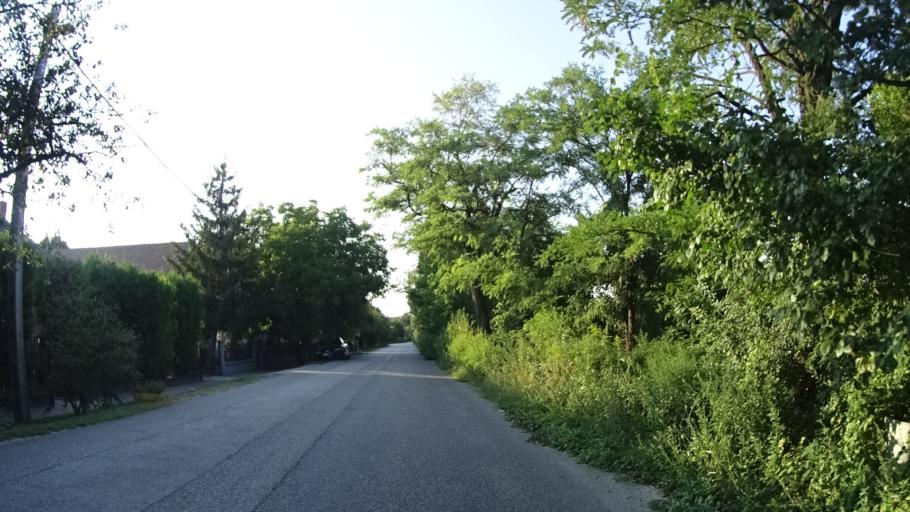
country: HU
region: Pest
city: Diosd
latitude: 47.3858
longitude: 18.9537
